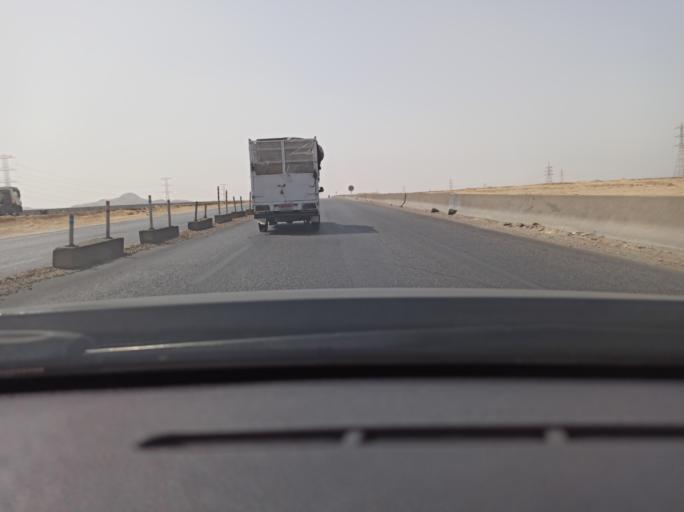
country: EG
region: Muhafazat Bani Suwayf
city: Bush
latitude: 29.1460
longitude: 31.2309
